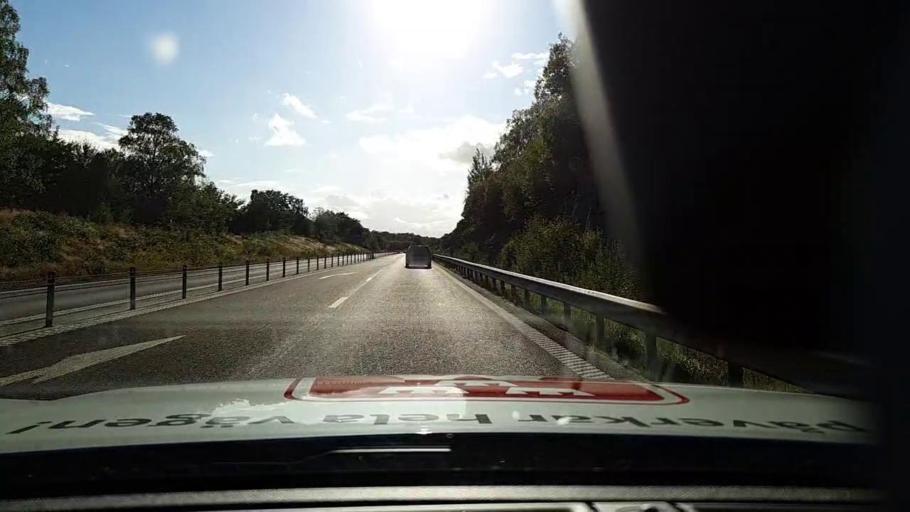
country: SE
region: Blekinge
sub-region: Ronneby Kommun
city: Brakne-Hoby
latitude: 56.2117
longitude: 15.0941
